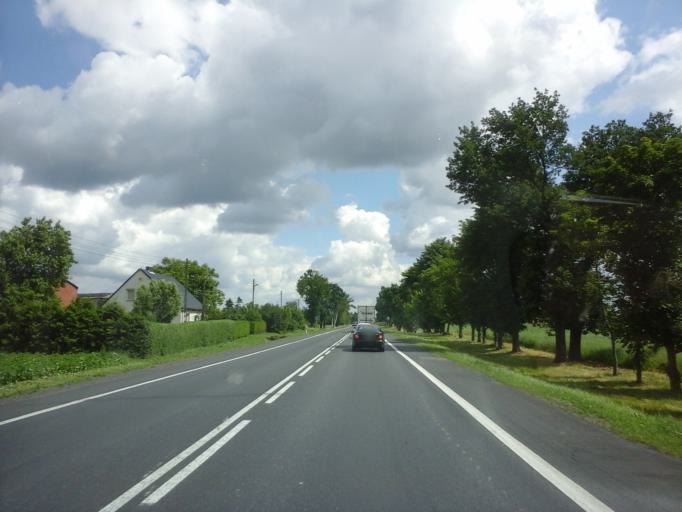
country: PL
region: West Pomeranian Voivodeship
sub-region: Powiat bialogardzki
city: Bialogard
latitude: 54.1268
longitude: 16.0193
